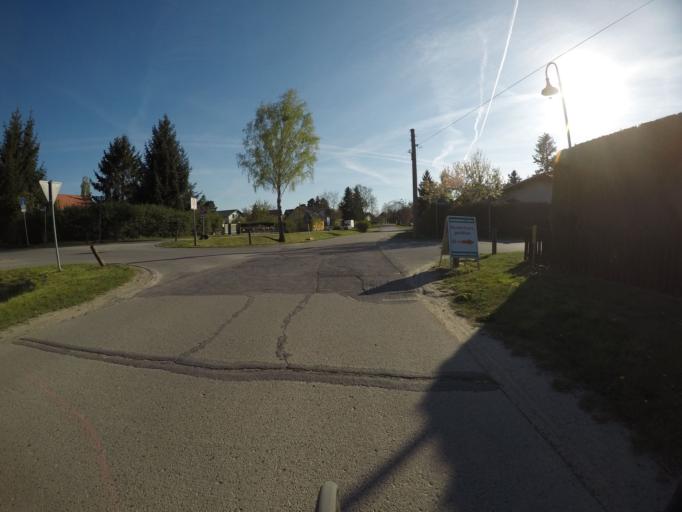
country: DE
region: Brandenburg
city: Neuenhagen
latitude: 52.5117
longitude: 13.7225
